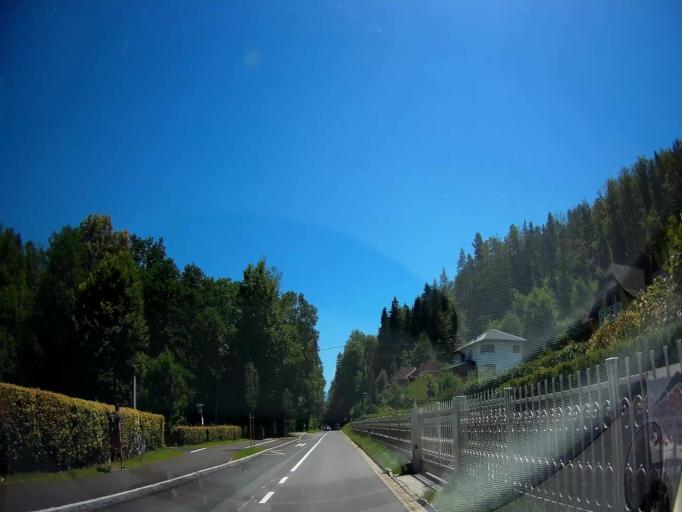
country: AT
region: Carinthia
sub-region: Politischer Bezirk Klagenfurt Land
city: Kottmannsdorf
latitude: 46.6108
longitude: 14.2435
